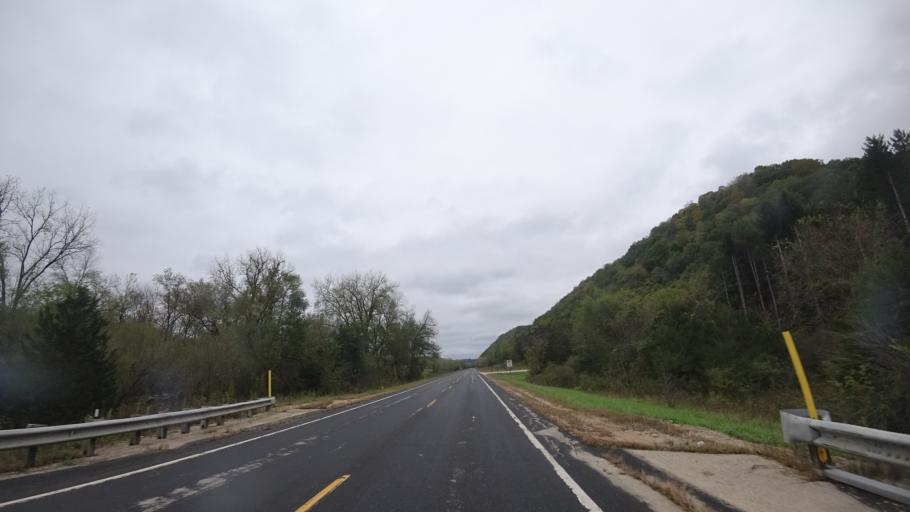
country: US
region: Wisconsin
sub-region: Grant County
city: Boscobel
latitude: 43.1899
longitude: -90.6653
